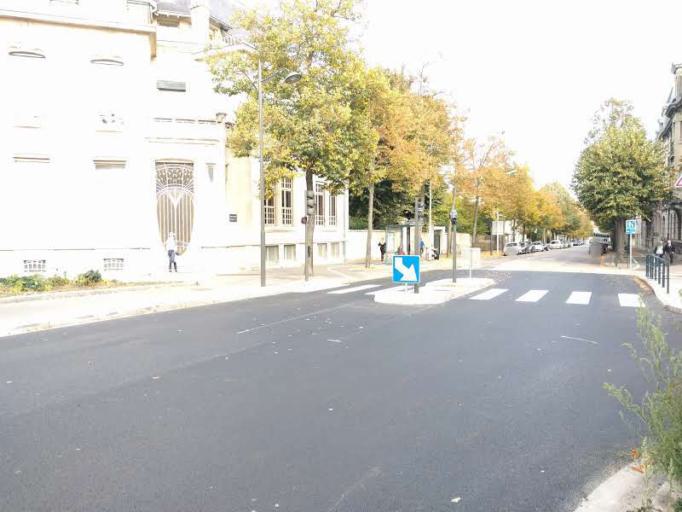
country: FR
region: Lorraine
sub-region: Departement de Meurthe-et-Moselle
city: Maxeville
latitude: 48.6982
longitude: 6.1752
